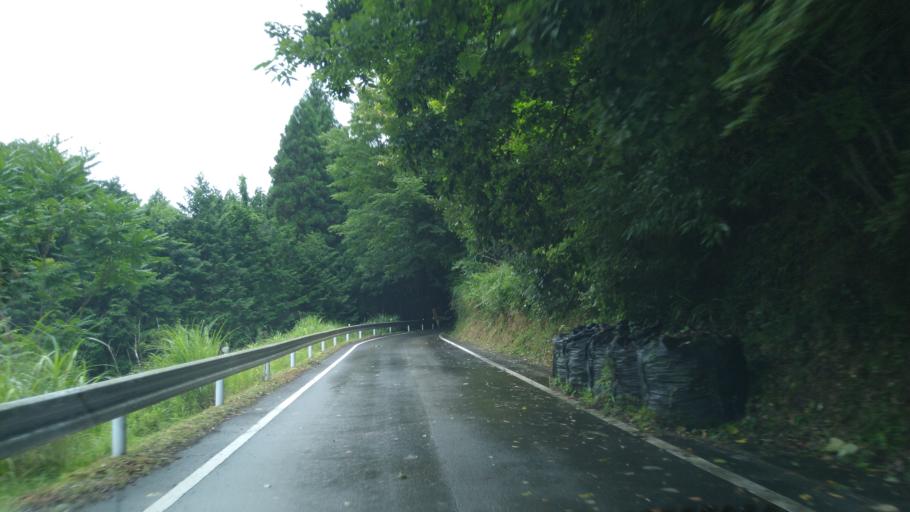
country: JP
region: Kyoto
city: Ayabe
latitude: 35.2382
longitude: 135.2654
